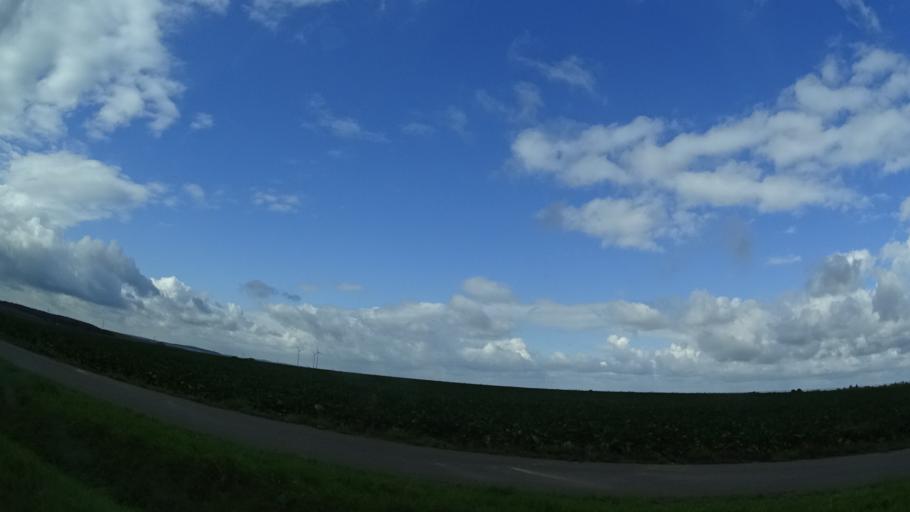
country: DE
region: Bavaria
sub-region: Regierungsbezirk Unterfranken
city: Lulsfeld
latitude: 49.8732
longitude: 10.3515
